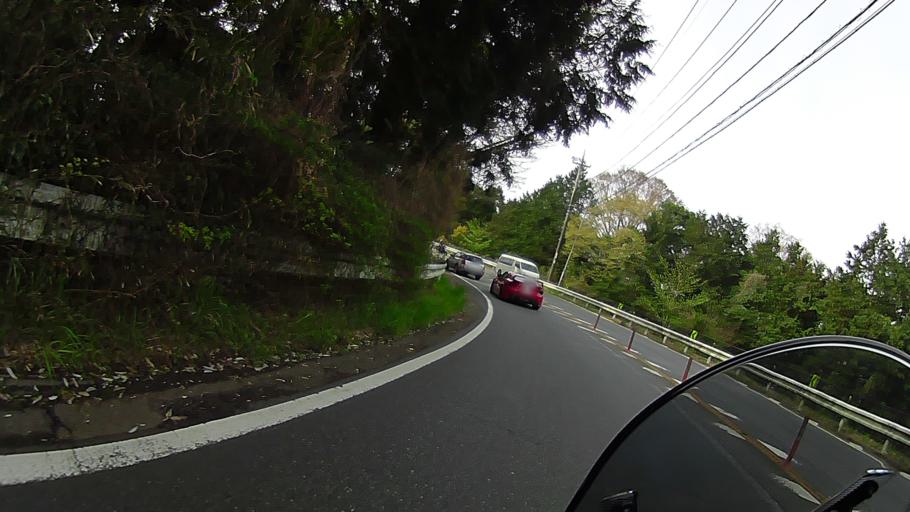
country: JP
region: Kanagawa
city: Hakone
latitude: 35.1479
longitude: 138.9781
